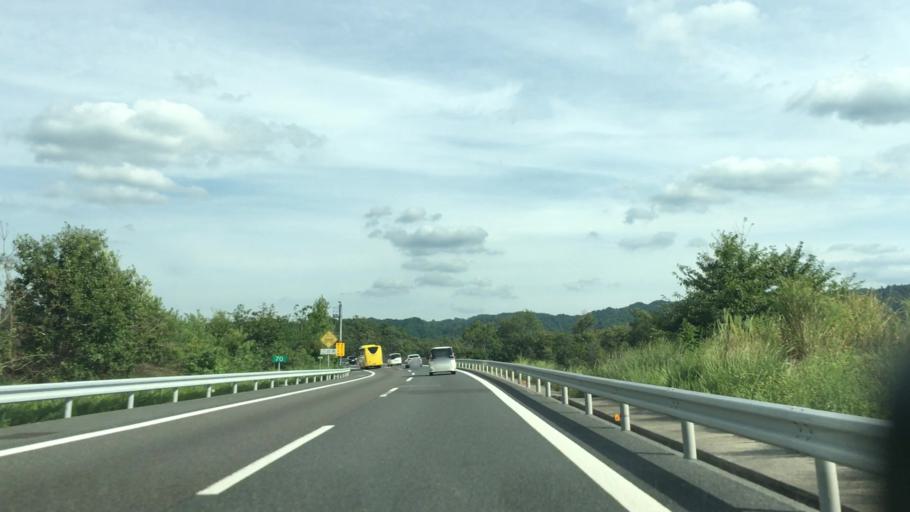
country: JP
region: Shiga Prefecture
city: Kusatsu
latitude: 34.9602
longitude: 135.9719
